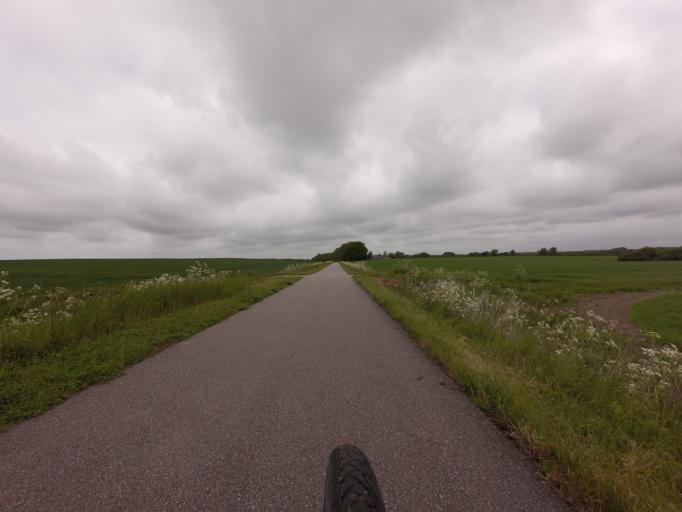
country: DK
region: Zealand
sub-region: Slagelse Kommune
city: Slagelse
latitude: 55.3660
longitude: 11.3852
